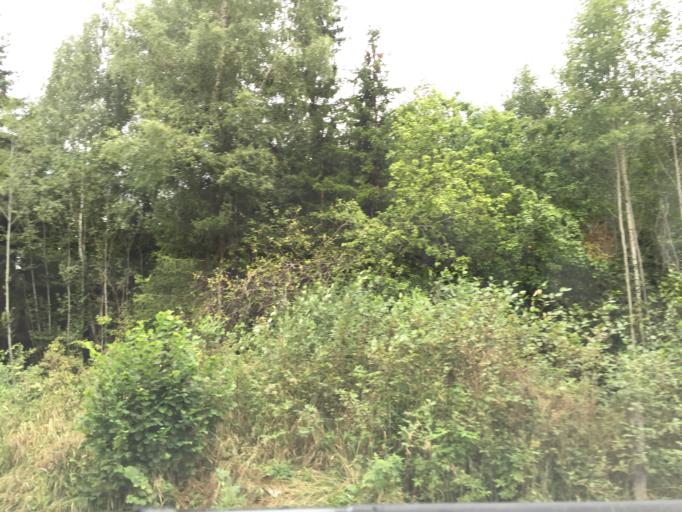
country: LV
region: Preilu Rajons
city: Jaunaglona
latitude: 56.2861
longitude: 27.0838
